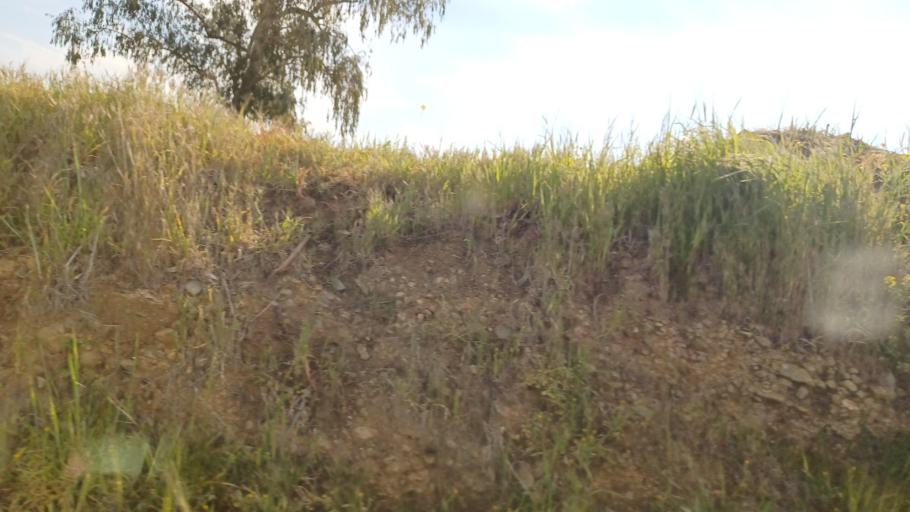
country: CY
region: Lefkosia
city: Kakopetria
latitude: 35.0774
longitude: 32.9532
